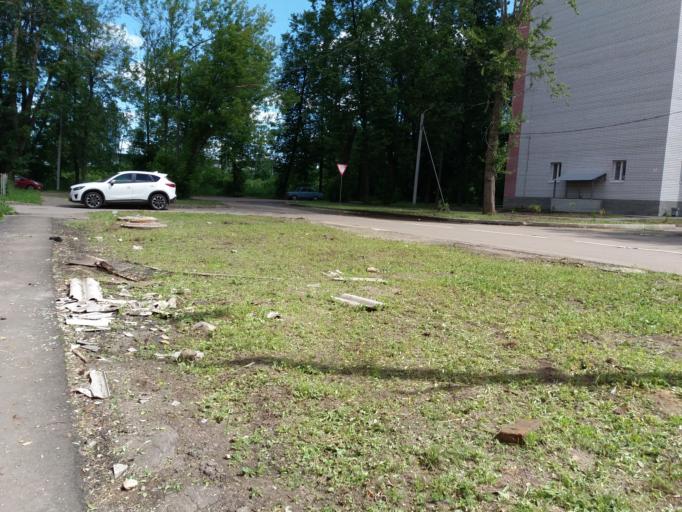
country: RU
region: Jaroslavl
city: Yaroslavl
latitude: 57.6419
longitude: 39.8439
